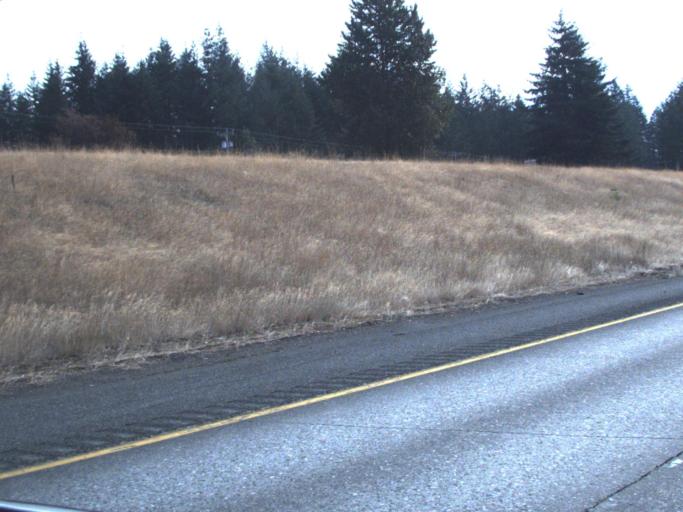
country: US
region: Washington
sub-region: King County
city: Tanner
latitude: 47.4696
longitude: -121.7296
